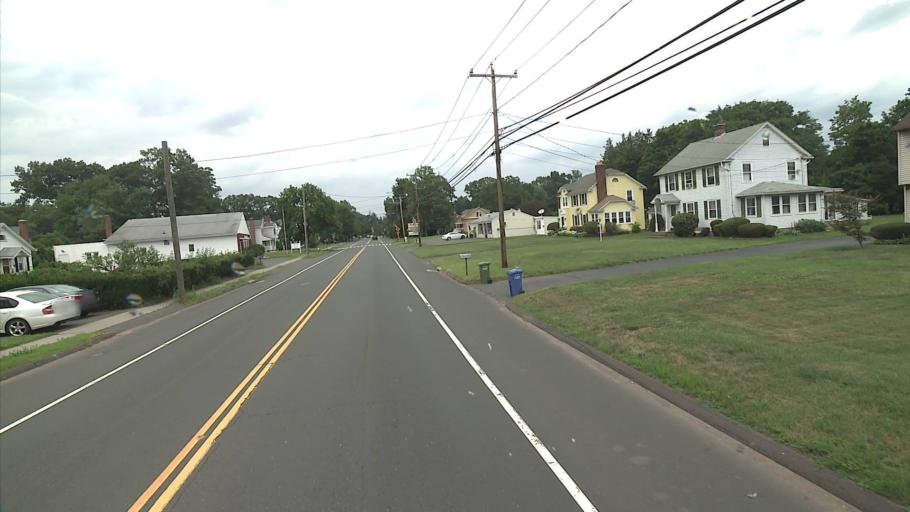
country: US
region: Connecticut
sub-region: Middlesex County
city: Cromwell
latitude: 41.6205
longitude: -72.6538
